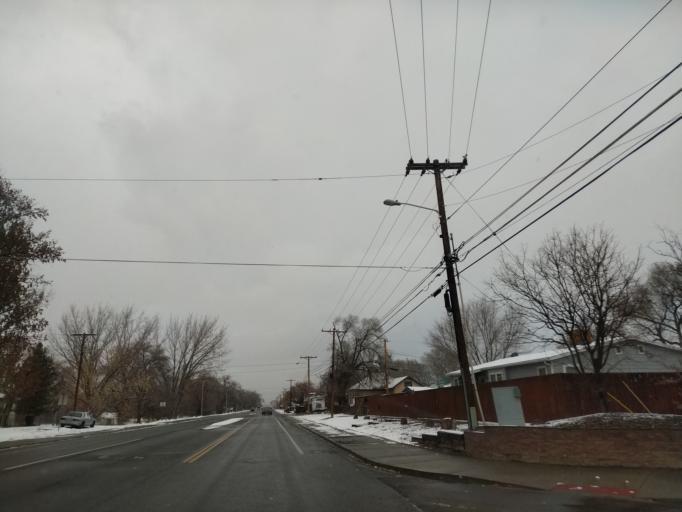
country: US
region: Colorado
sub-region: Montrose County
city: Montrose
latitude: 38.4789
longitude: -107.8834
